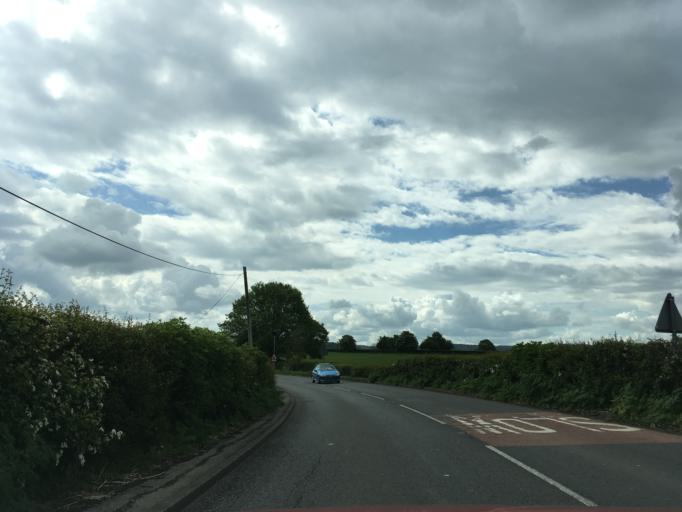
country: GB
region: England
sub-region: Gloucestershire
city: Stonehouse
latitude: 51.7699
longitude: -2.2828
